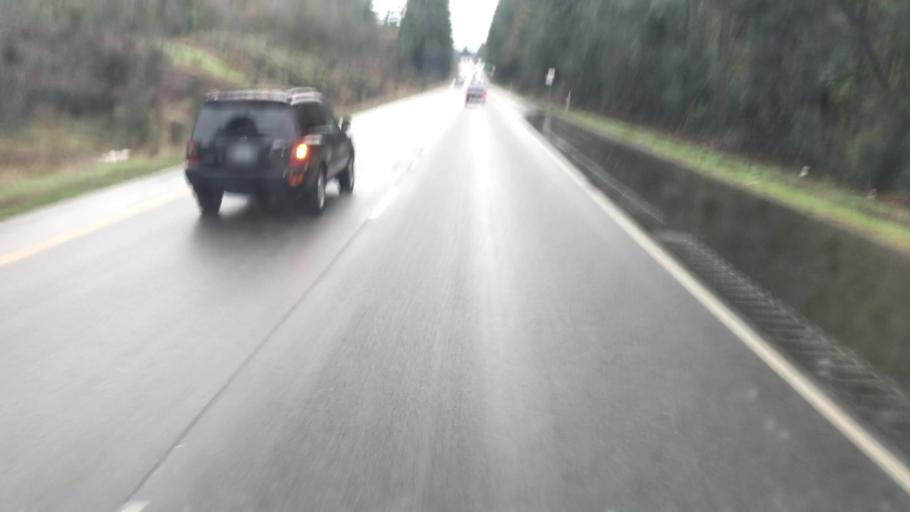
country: US
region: Washington
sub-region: Kitsap County
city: Burley
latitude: 47.4424
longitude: -122.6228
